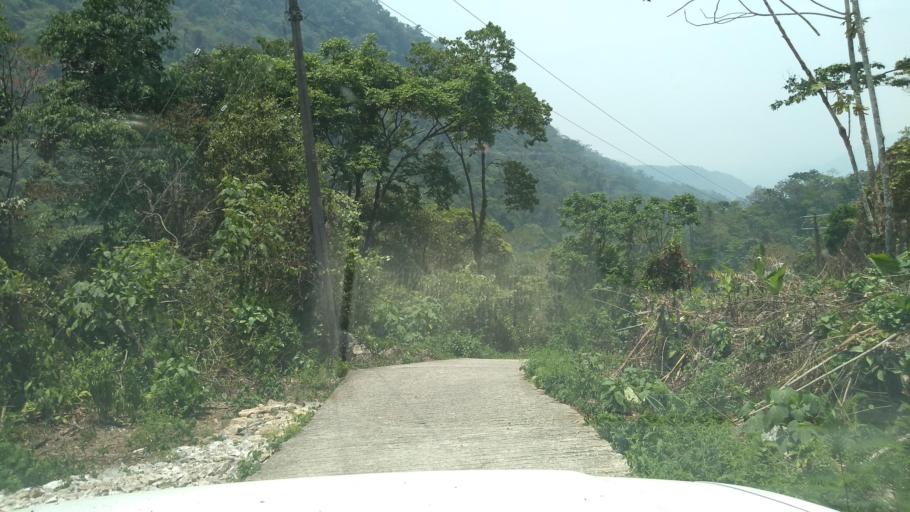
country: MX
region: Veracruz
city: Motzorongo
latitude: 18.6004
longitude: -96.7483
